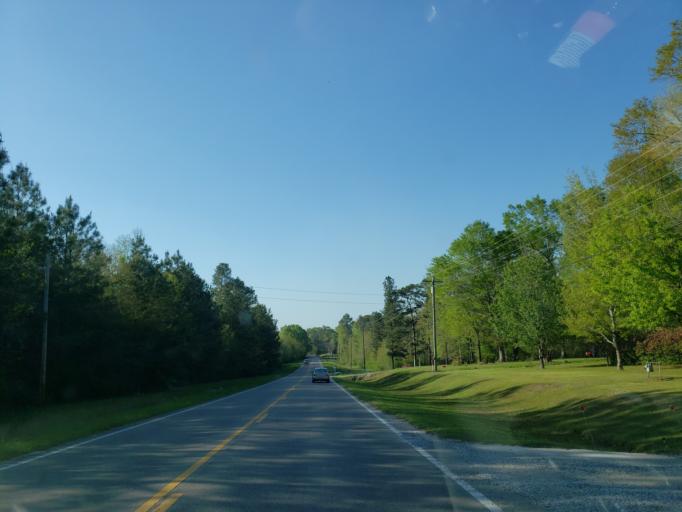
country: US
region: Mississippi
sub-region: Jones County
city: Laurel
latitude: 31.6424
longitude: -89.0972
